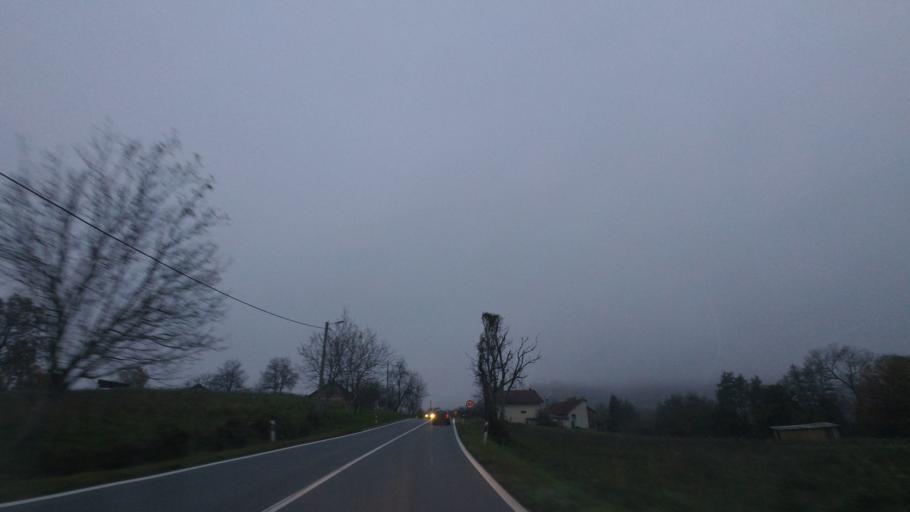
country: HR
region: Sisacko-Moslavacka
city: Petrinja
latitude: 45.4341
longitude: 16.2316
